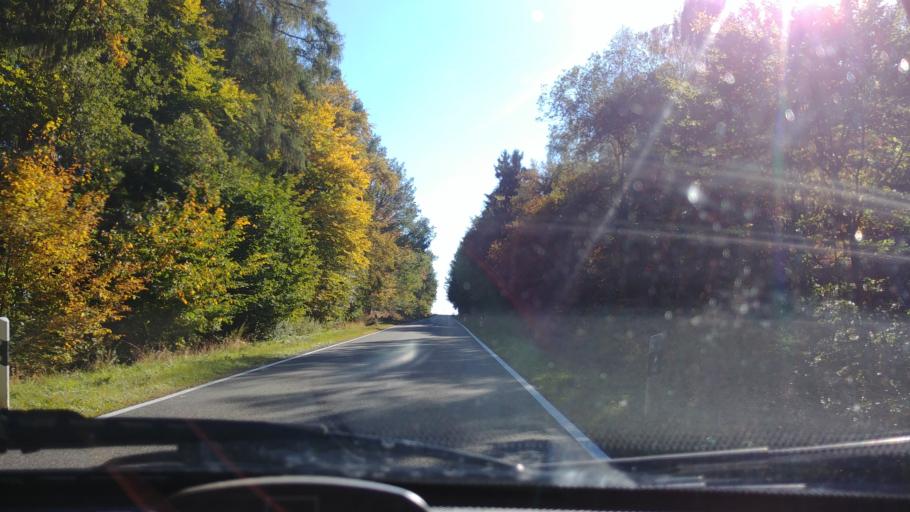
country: DE
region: Hesse
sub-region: Regierungsbezirk Darmstadt
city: Bad Schwalbach
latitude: 50.1692
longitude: 8.1039
